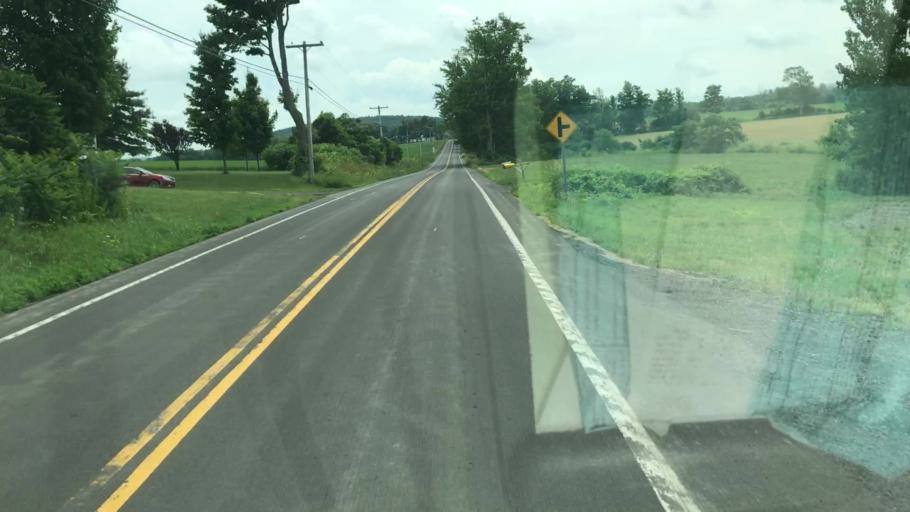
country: US
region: New York
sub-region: Onondaga County
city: Manlius
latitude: 42.9302
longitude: -75.9765
